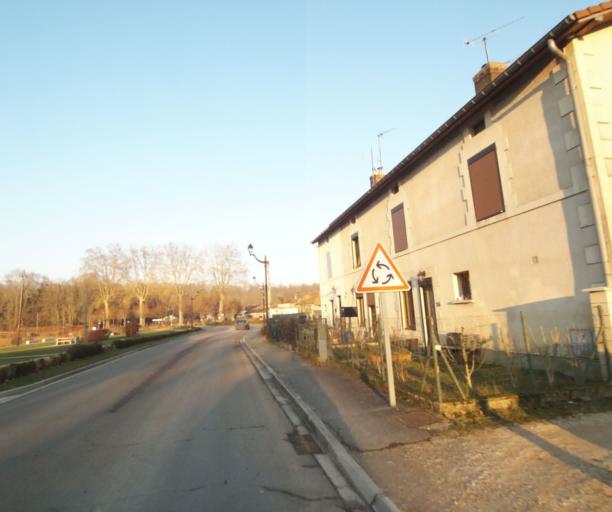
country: FR
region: Champagne-Ardenne
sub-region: Departement de la Haute-Marne
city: Bienville
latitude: 48.6074
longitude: 5.0440
